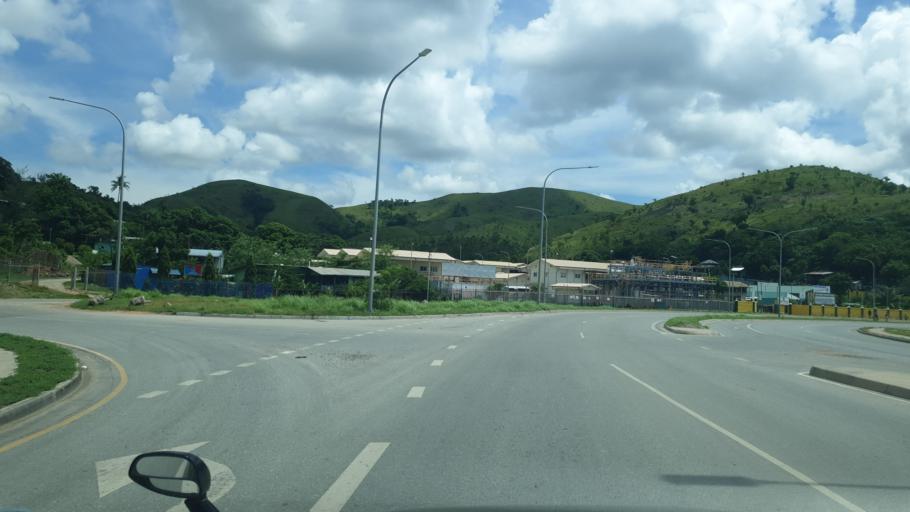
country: PG
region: National Capital
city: Port Moresby
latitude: -9.4459
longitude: 147.1435
